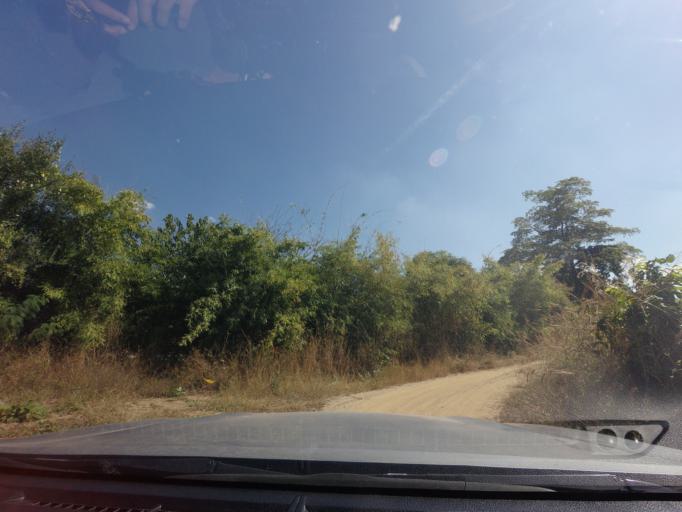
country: TH
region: Lampang
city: Mae Mo
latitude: 18.4725
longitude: 99.6320
